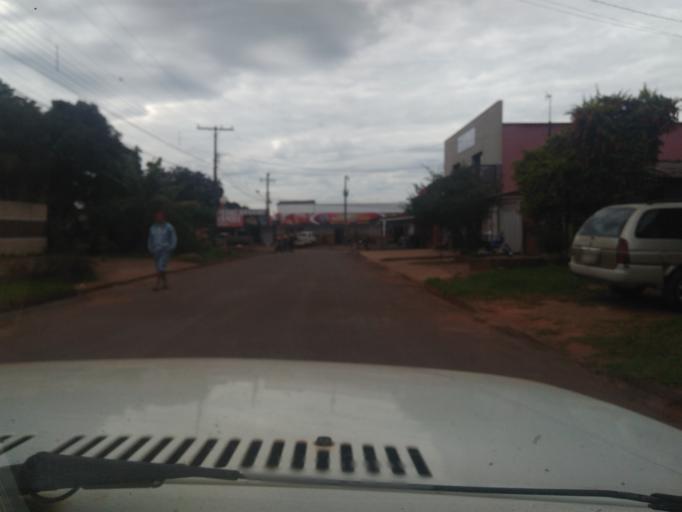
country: BR
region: Mato Grosso do Sul
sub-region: Ponta Pora
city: Ponta Pora
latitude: -22.5097
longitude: -55.7317
